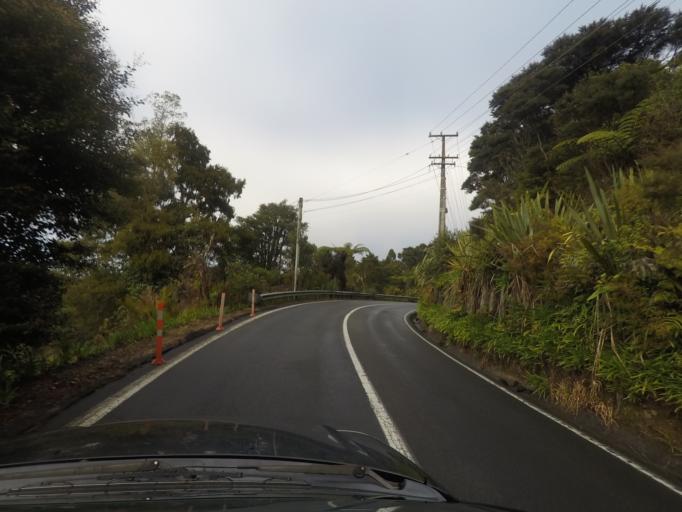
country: NZ
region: Auckland
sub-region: Auckland
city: Titirangi
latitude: -36.9228
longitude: 174.5839
